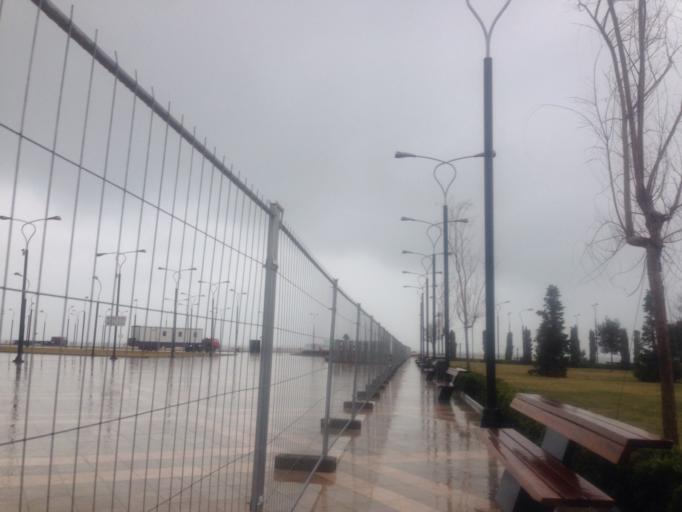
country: AZ
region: Baki
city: Badamdar
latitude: 40.3439
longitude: 49.8481
